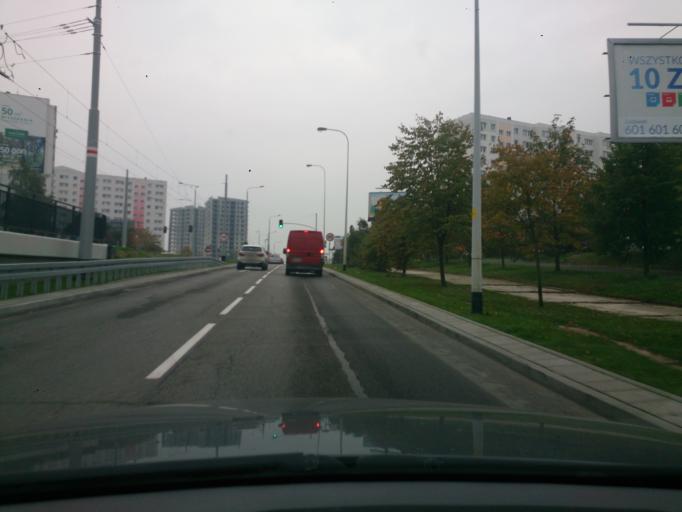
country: PL
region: Pomeranian Voivodeship
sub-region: Powiat gdanski
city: Kowale
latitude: 54.3615
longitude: 18.5758
